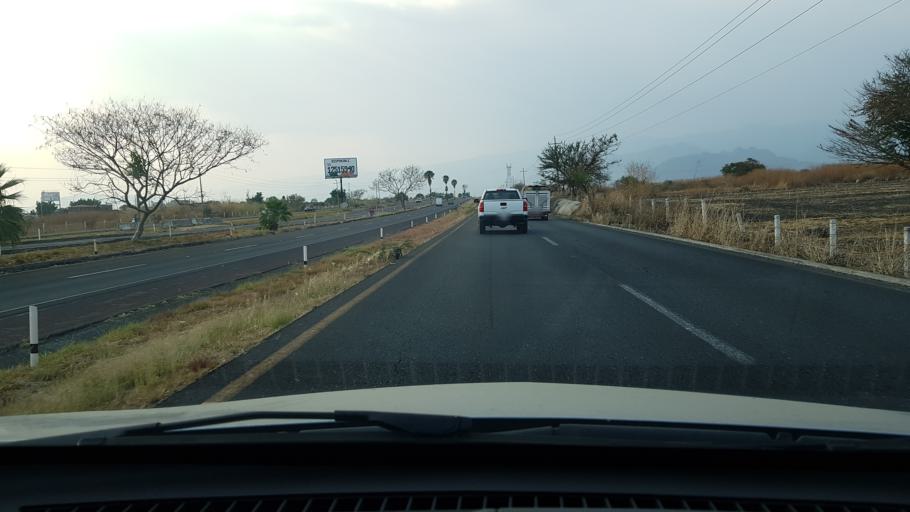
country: MX
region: Morelos
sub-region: Cuautla
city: Tierra Larga (Campo Nuevo)
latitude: 18.8718
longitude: -98.9557
